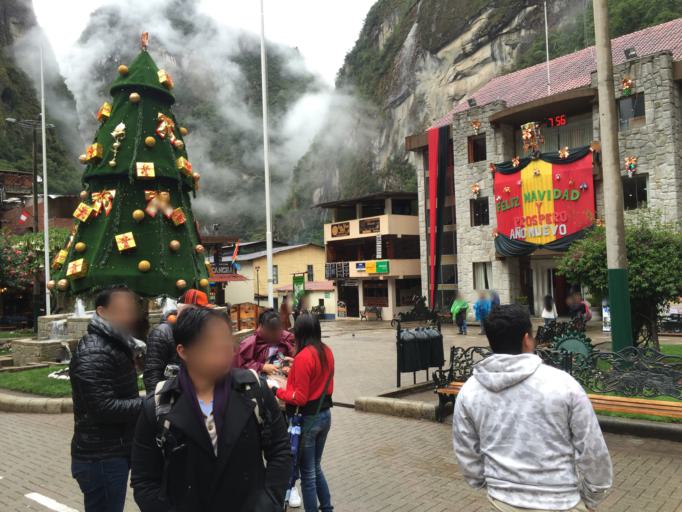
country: PE
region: Cusco
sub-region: Provincia de La Convencion
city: Santa Teresa
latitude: -13.1543
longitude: -72.5255
